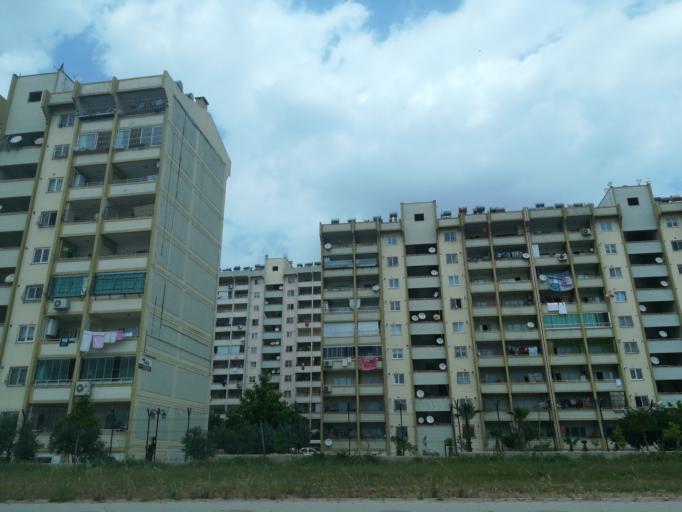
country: TR
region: Adana
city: Seyhan
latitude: 37.0027
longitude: 35.2419
